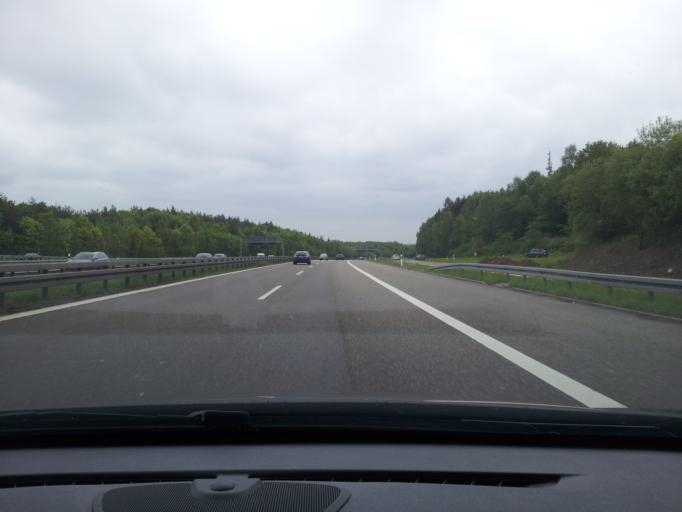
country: DE
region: Baden-Wuerttemberg
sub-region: Regierungsbezirk Stuttgart
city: Sindelfingen
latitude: 48.7272
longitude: 9.0707
